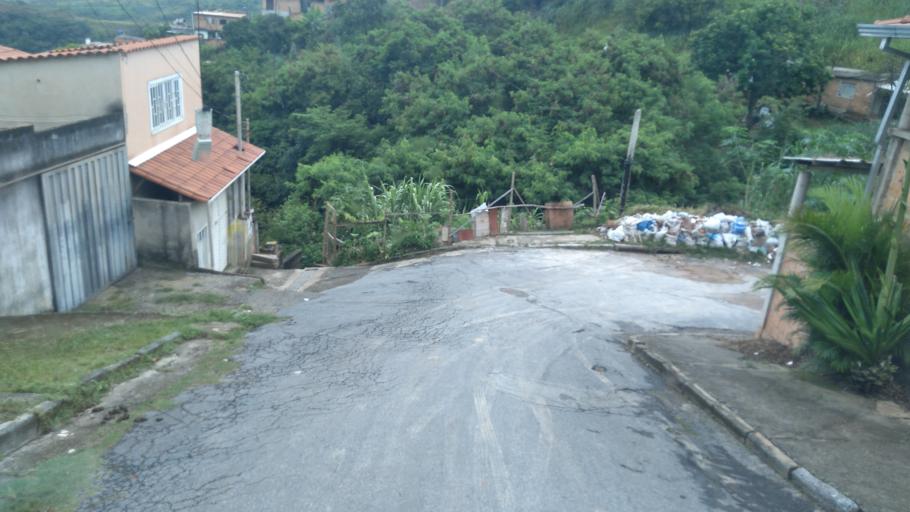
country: BR
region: Minas Gerais
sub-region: Belo Horizonte
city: Belo Horizonte
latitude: -19.9139
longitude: -43.8837
